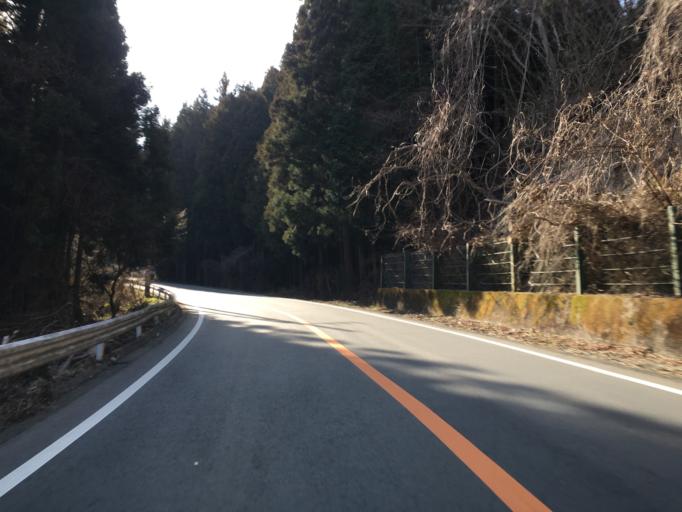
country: JP
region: Ibaraki
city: Takahagi
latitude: 36.7404
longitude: 140.5693
